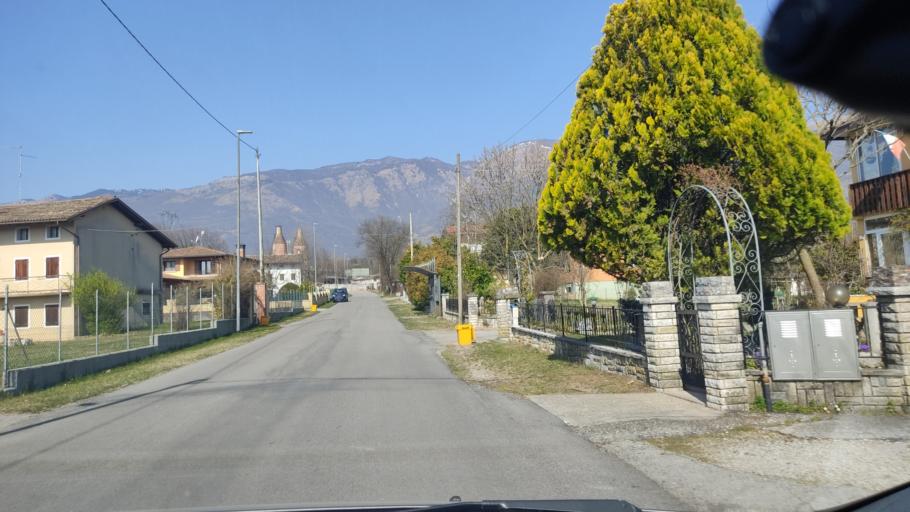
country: IT
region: Friuli Venezia Giulia
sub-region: Provincia di Pordenone
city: Budoia
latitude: 46.0517
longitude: 12.5584
